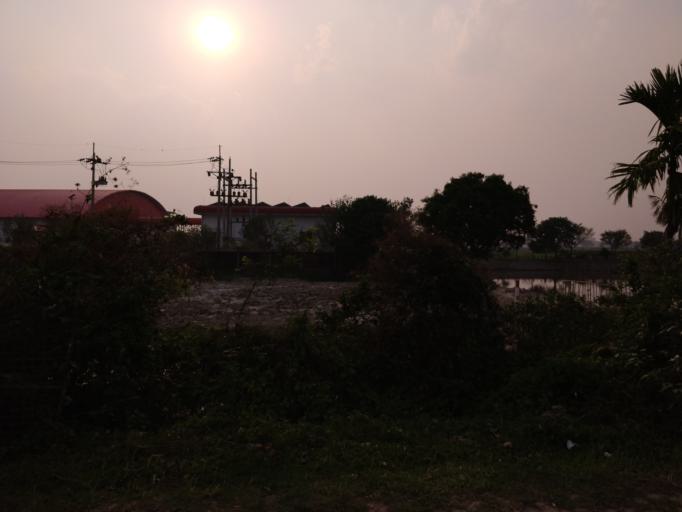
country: BD
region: Sylhet
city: Habiganj
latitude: 24.1360
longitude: 91.3517
